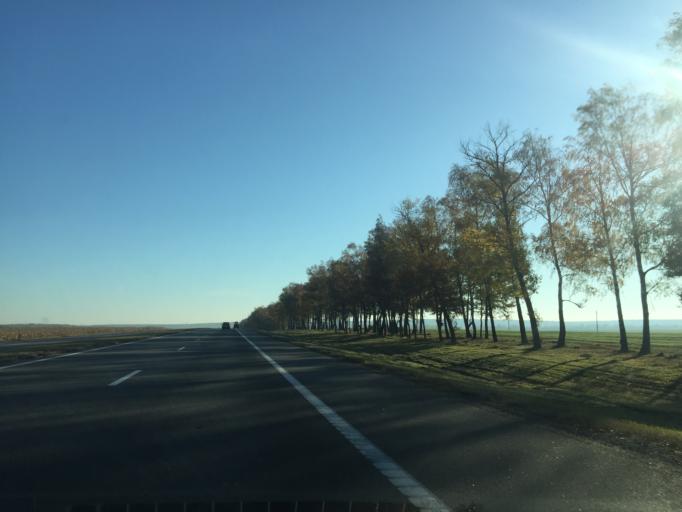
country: BY
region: Minsk
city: Smilavichy
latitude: 53.7609
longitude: 28.0534
